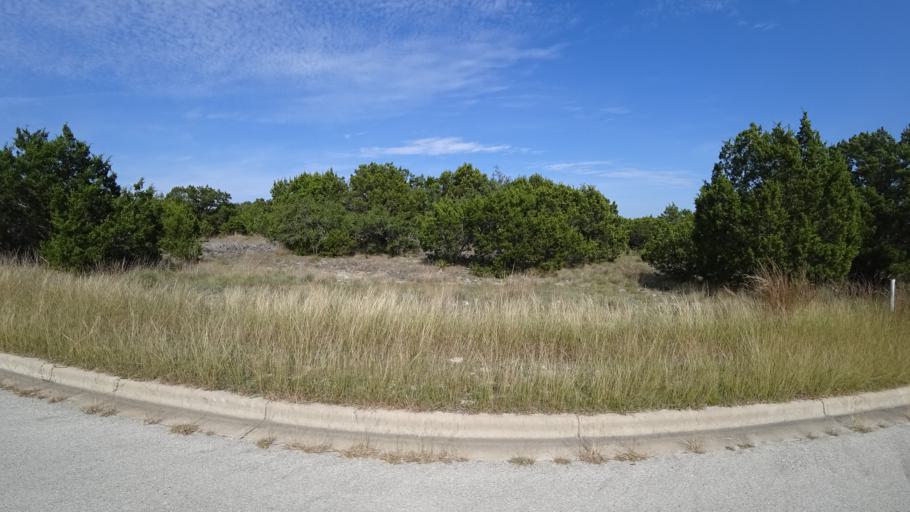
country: US
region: Texas
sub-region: Travis County
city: Bee Cave
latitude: 30.2275
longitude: -97.9319
